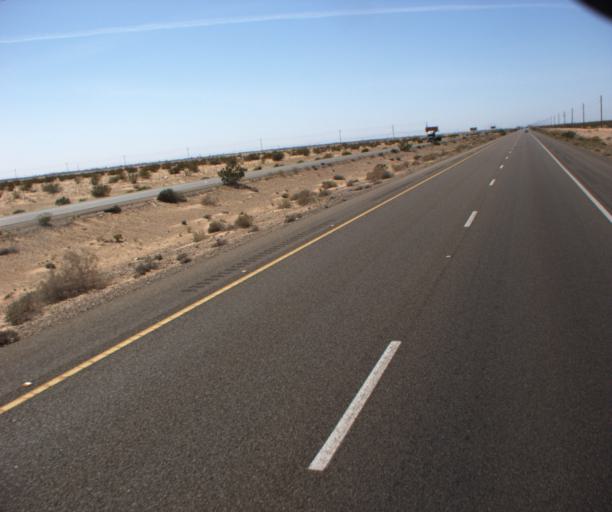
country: MX
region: Sonora
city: San Luis Rio Colorado
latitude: 32.4947
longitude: -114.6788
